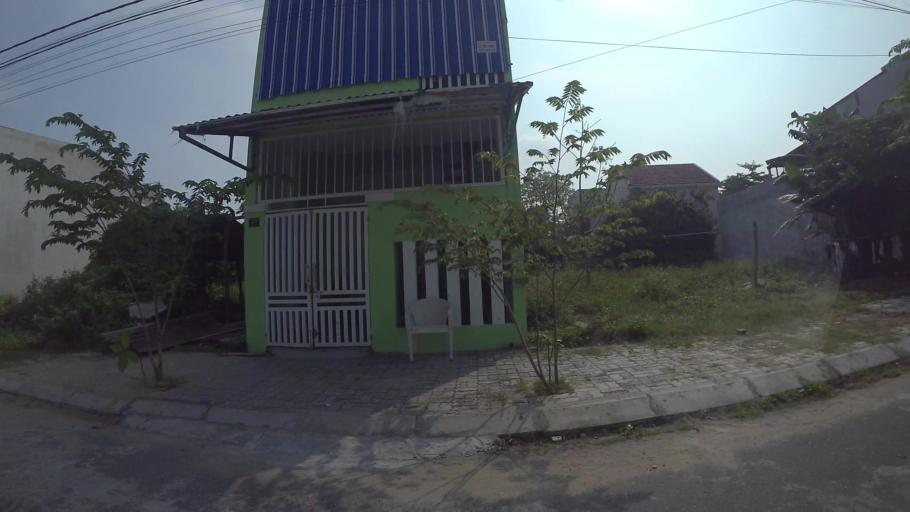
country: VN
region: Da Nang
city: Ngu Hanh Son
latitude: 16.0292
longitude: 108.2436
